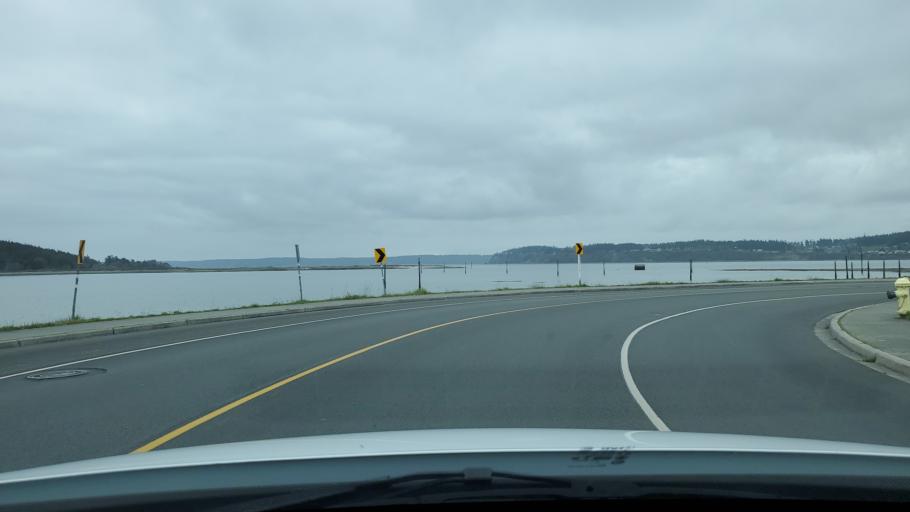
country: US
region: Washington
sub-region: Island County
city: Oak Harbor
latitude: 48.2887
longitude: -122.6440
